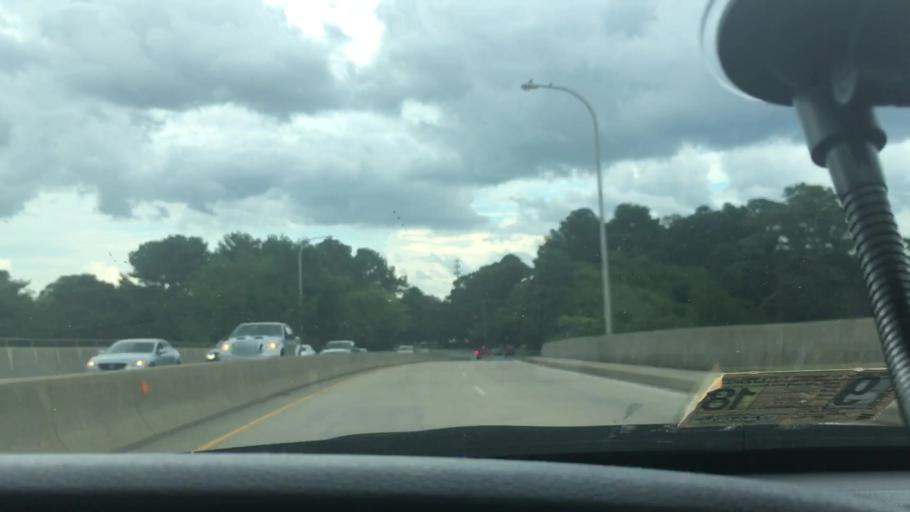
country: US
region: Virginia
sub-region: City of Portsmouth
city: Portsmouth Heights
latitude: 36.8235
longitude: -76.3977
